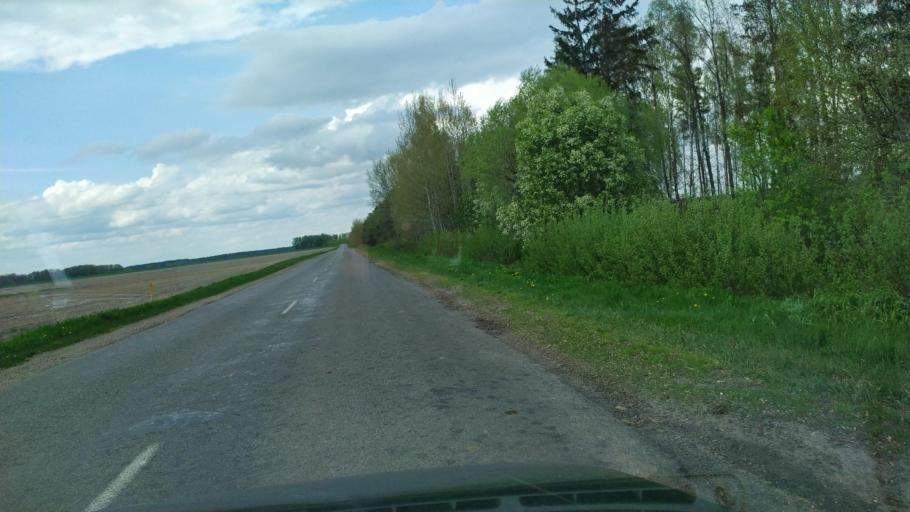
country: BY
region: Brest
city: Pruzhany
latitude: 52.6592
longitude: 24.3813
